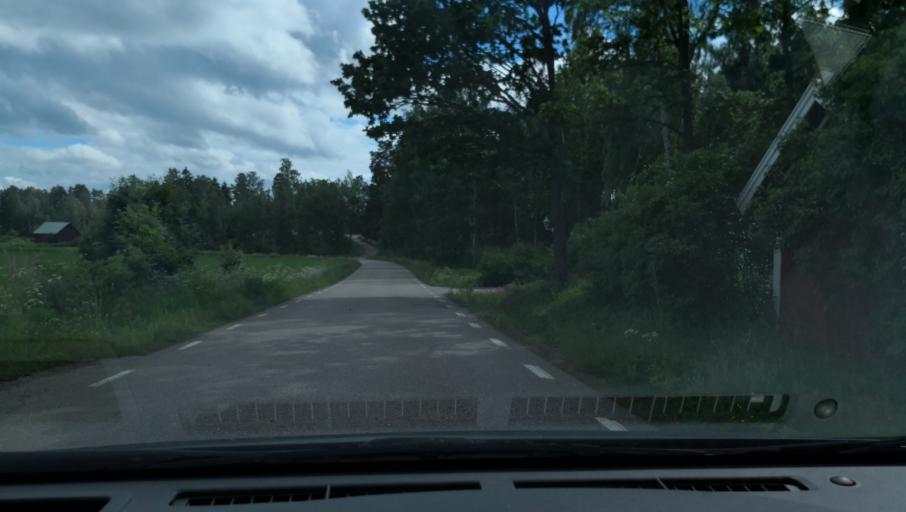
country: SE
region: OErebro
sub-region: Lindesbergs Kommun
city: Fellingsbro
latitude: 59.3121
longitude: 15.6778
